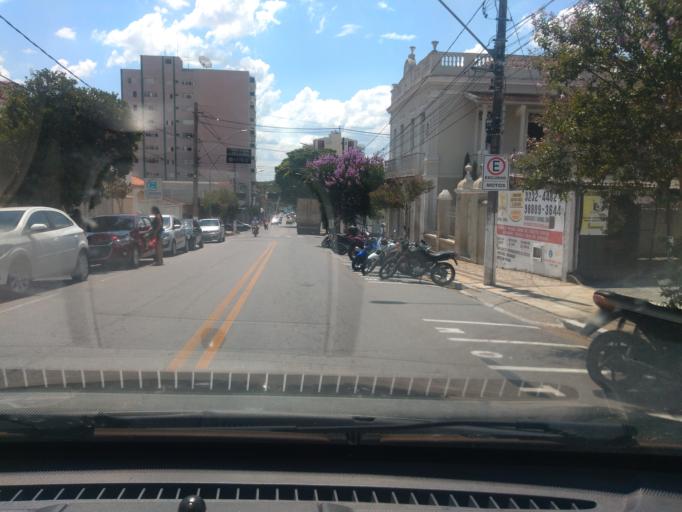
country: BR
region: Minas Gerais
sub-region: Tres Coracoes
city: Tres Coracoes
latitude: -21.6990
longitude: -45.2538
